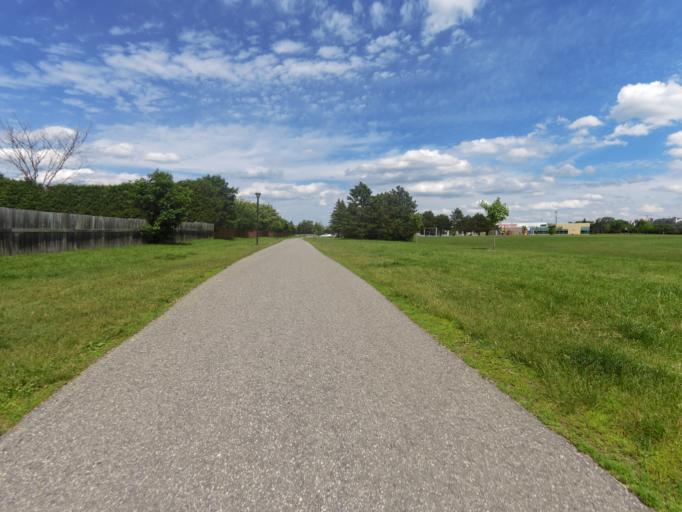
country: CA
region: Ontario
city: Ottawa
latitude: 45.3631
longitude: -75.6382
